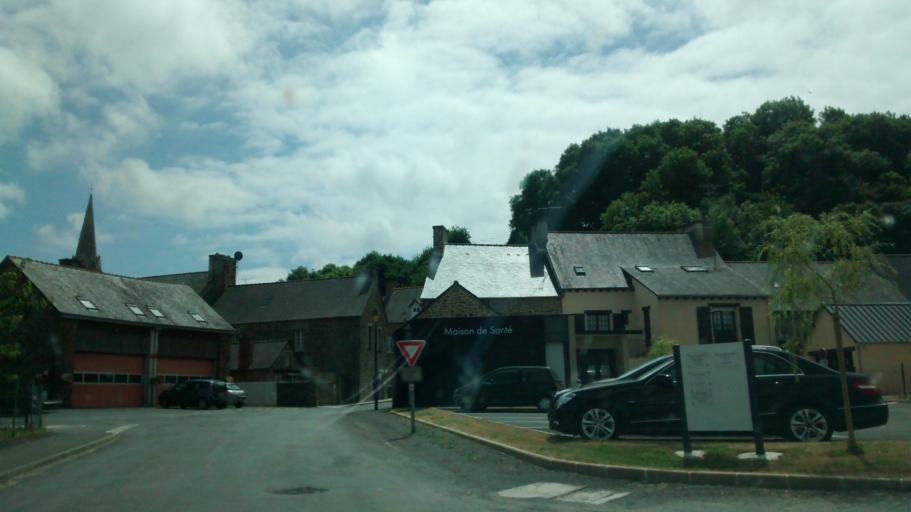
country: FR
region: Brittany
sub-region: Departement d'Ille-et-Vilaine
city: Saint-Broladre
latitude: 48.5873
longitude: -1.6585
